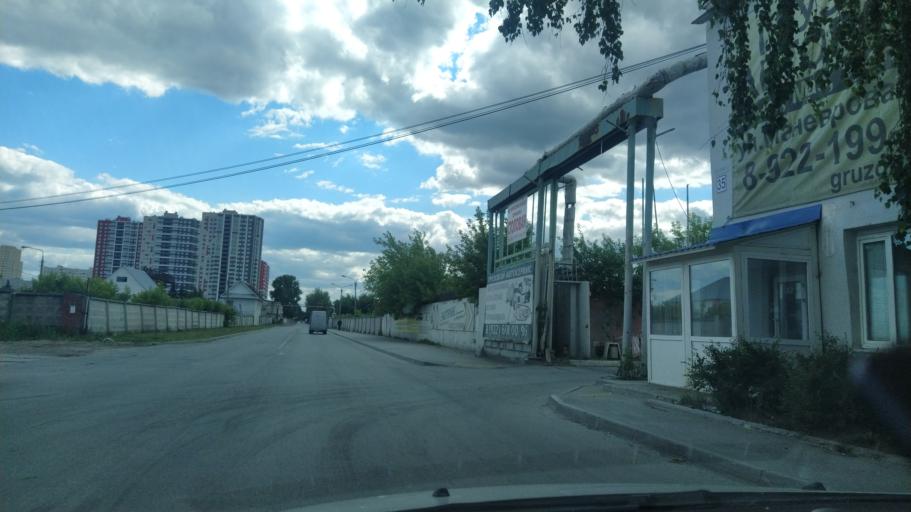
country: RU
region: Sverdlovsk
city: Shuvakish
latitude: 56.8816
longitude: 60.5285
